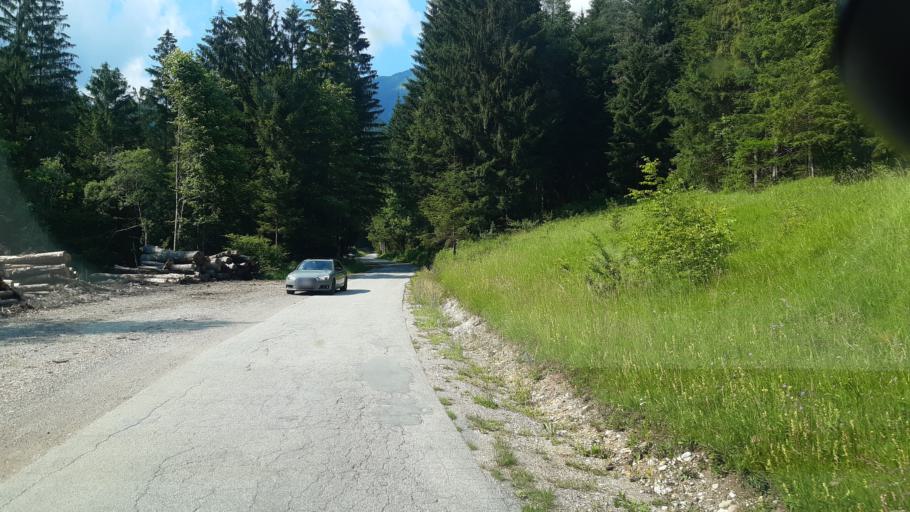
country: SI
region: Radovljica
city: Radovljica
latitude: 46.3843
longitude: 14.2179
